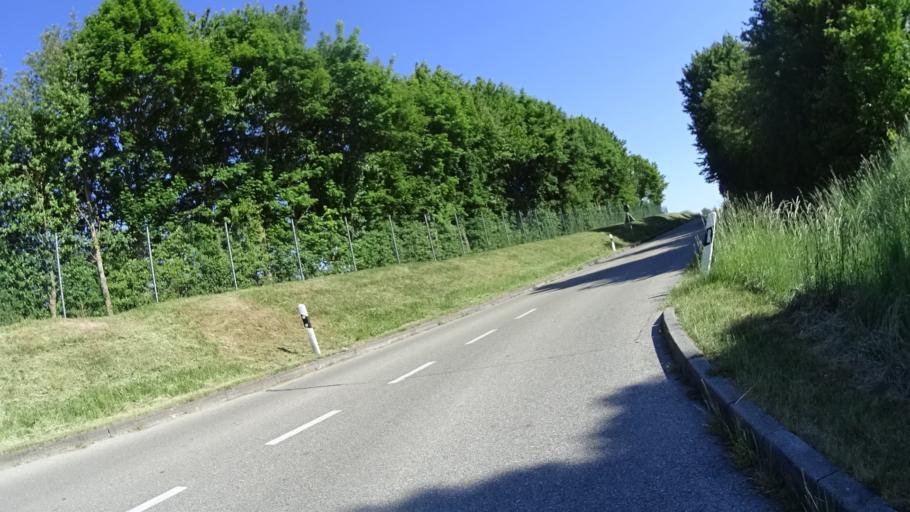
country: DE
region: Bavaria
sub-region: Regierungsbezirk Mittelfranken
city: Dombuhl
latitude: 49.2103
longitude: 10.3132
